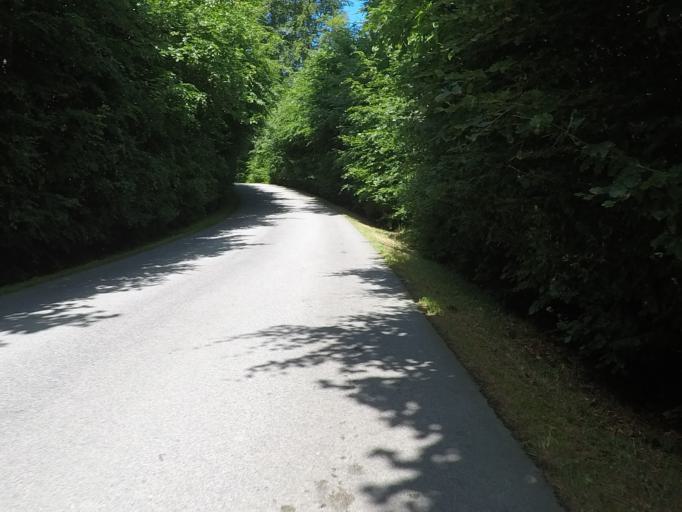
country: SE
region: Skane
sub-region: Svedala Kommun
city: Klagerup
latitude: 55.5582
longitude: 13.2174
